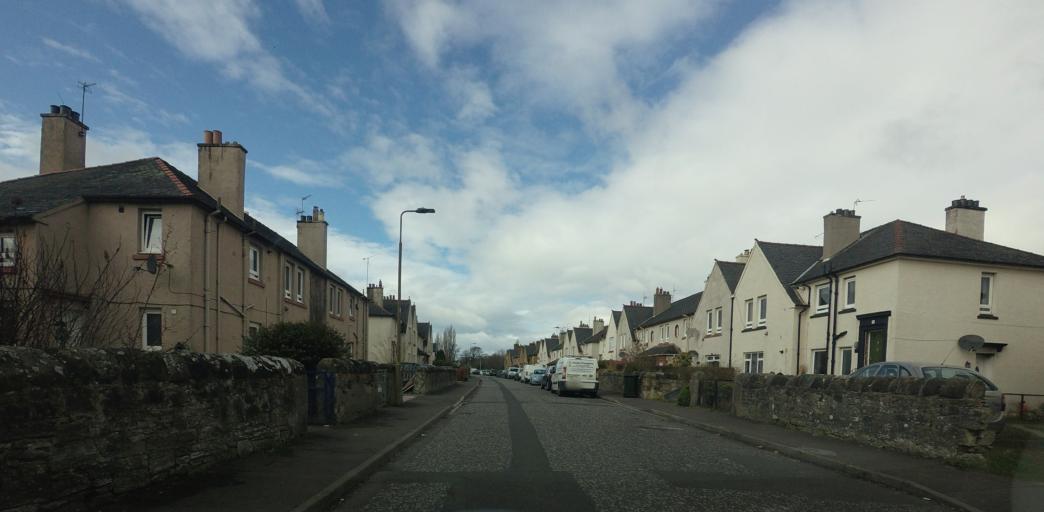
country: GB
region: Scotland
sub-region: Edinburgh
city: Queensferry
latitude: 55.9908
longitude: -3.4074
